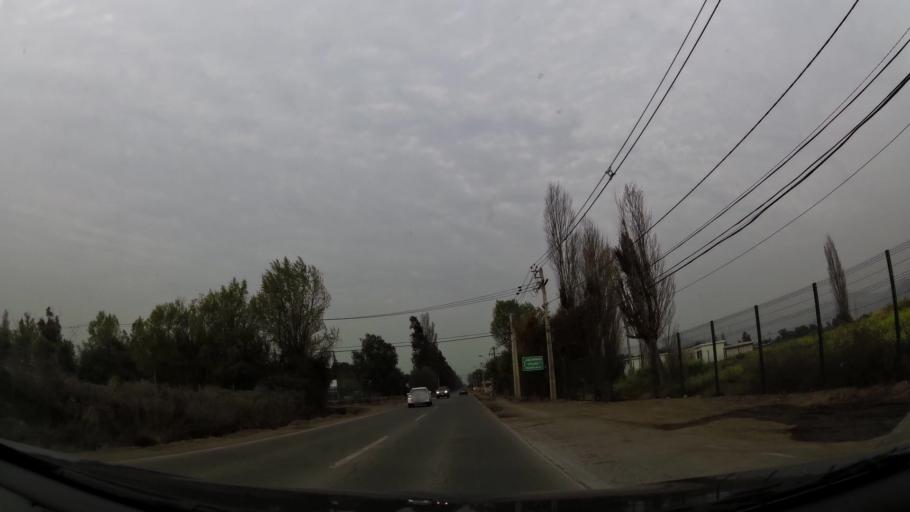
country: CL
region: Santiago Metropolitan
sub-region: Provincia de Chacabuco
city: Chicureo Abajo
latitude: -33.2856
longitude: -70.6963
